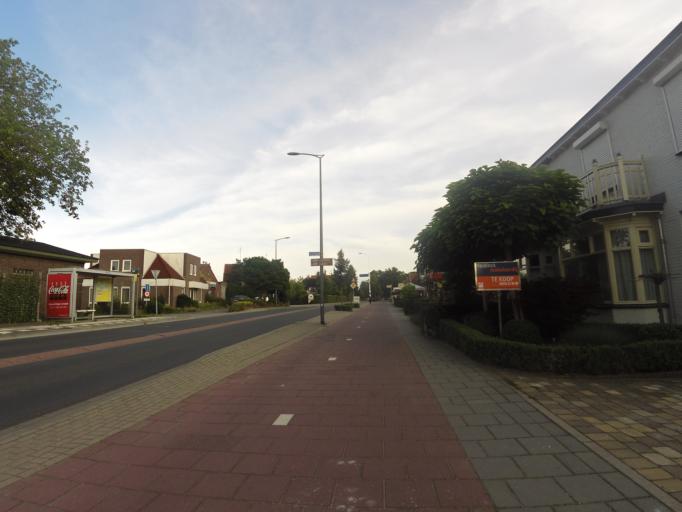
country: NL
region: Gelderland
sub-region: Oude IJsselstreek
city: Gendringen
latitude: 51.9167
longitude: 6.3747
